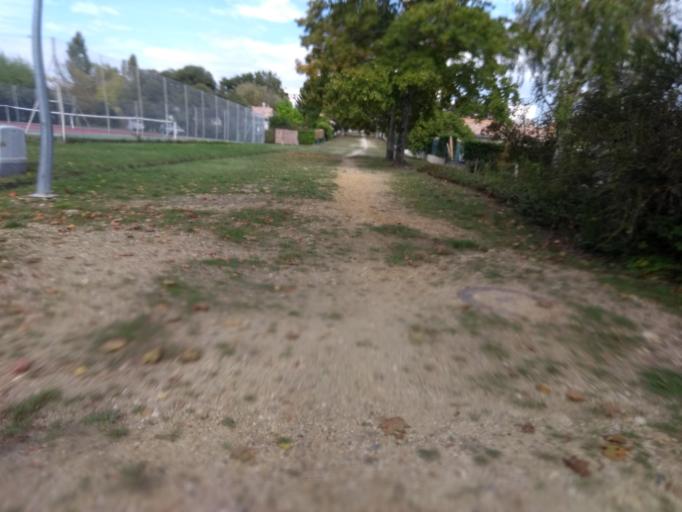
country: FR
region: Aquitaine
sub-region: Departement de la Gironde
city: Gradignan
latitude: 44.7693
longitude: -0.6218
